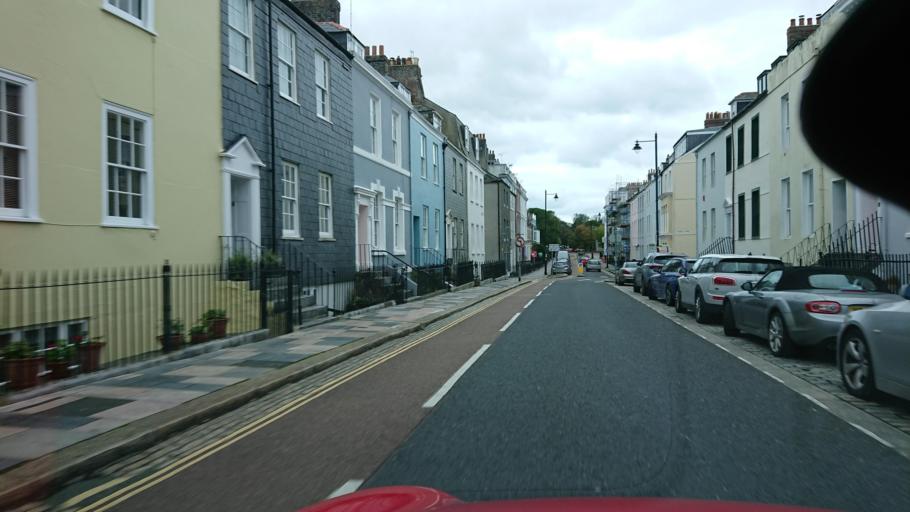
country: GB
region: England
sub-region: Plymouth
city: Plymouth
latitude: 50.3652
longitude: -4.1617
